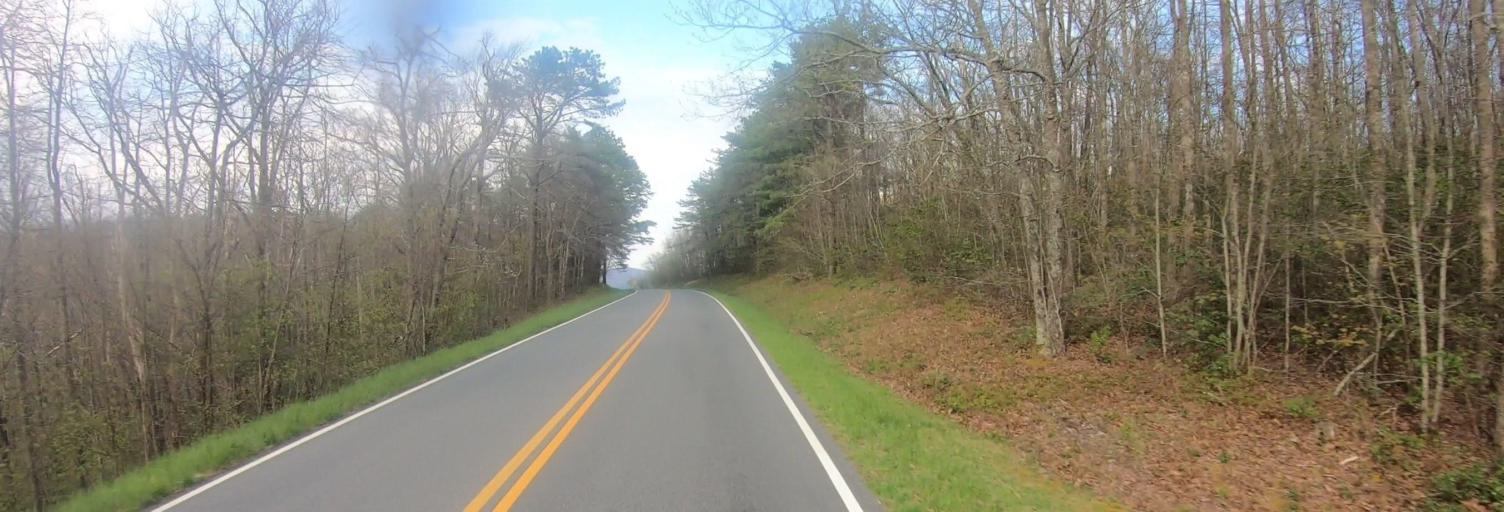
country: US
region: Virginia
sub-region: Augusta County
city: Crimora
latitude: 38.1620
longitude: -78.7717
